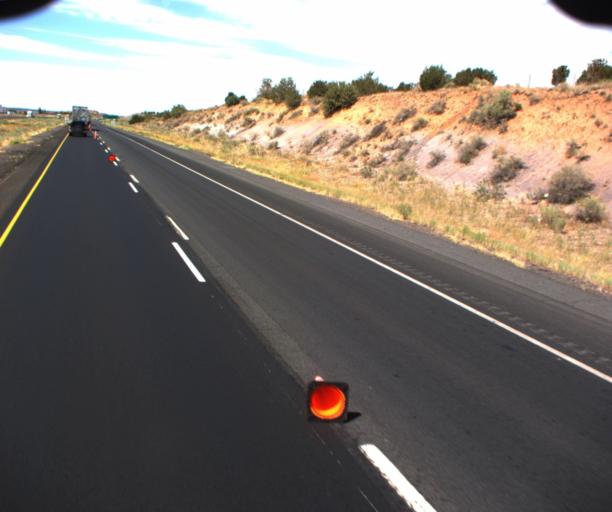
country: US
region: Arizona
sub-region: Apache County
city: Houck
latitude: 35.3310
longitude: -109.0758
